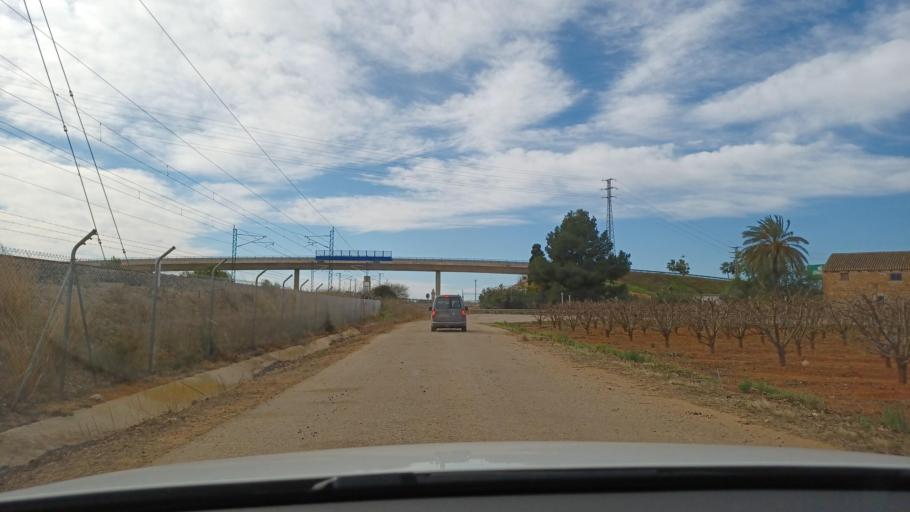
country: ES
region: Valencia
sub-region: Provincia de Valencia
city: Benifaio
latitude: 39.2896
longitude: -0.4387
